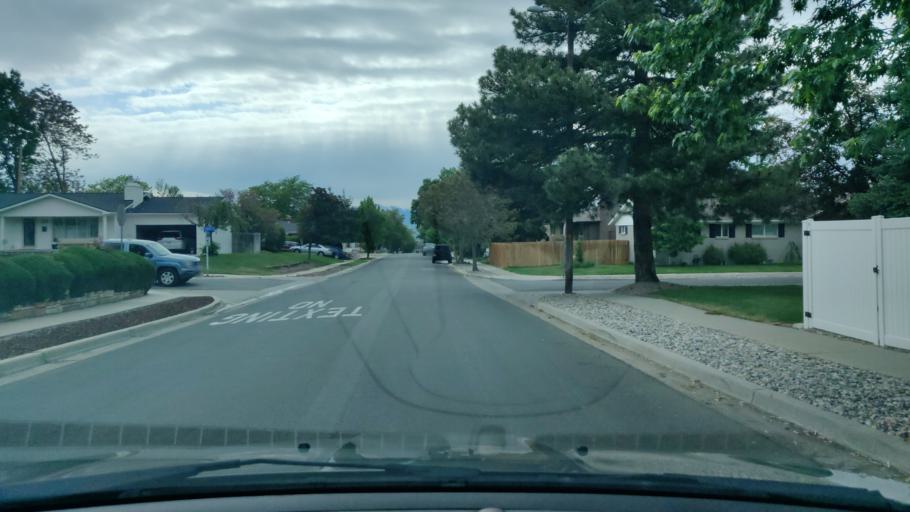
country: US
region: Utah
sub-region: Salt Lake County
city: Cottonwood Heights
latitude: 40.6292
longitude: -111.8210
